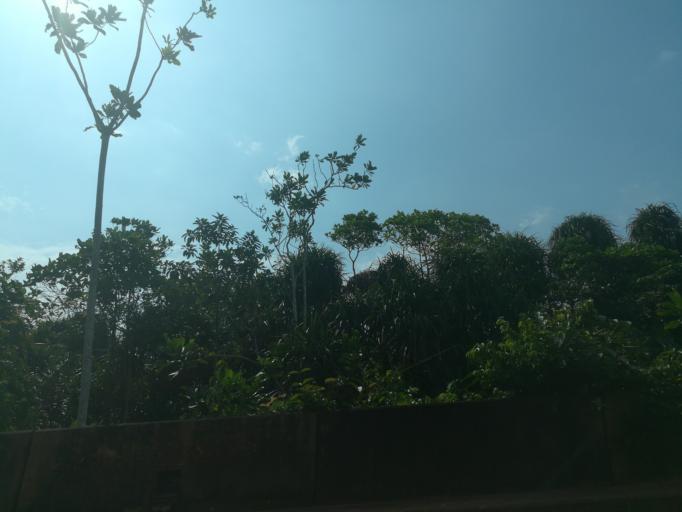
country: NG
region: Lagos
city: Ikorodu
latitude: 6.6291
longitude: 3.6657
